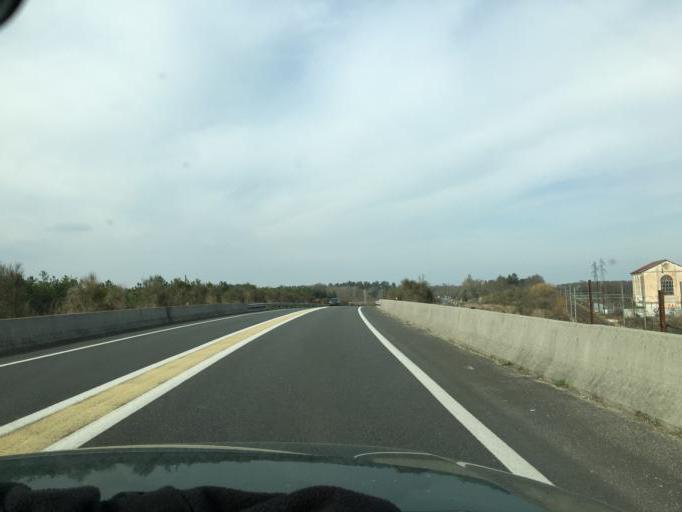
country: FR
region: Centre
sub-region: Departement du Loiret
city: La Ferte-Saint-Aubin
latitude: 47.7673
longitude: 1.9373
